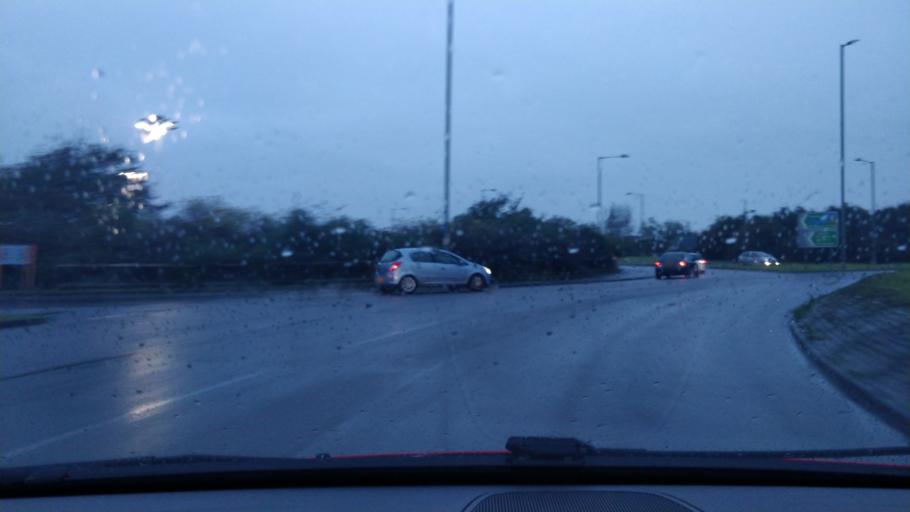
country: GB
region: England
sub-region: Lancashire
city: Poulton le Fylde
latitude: 53.7897
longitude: -2.9827
